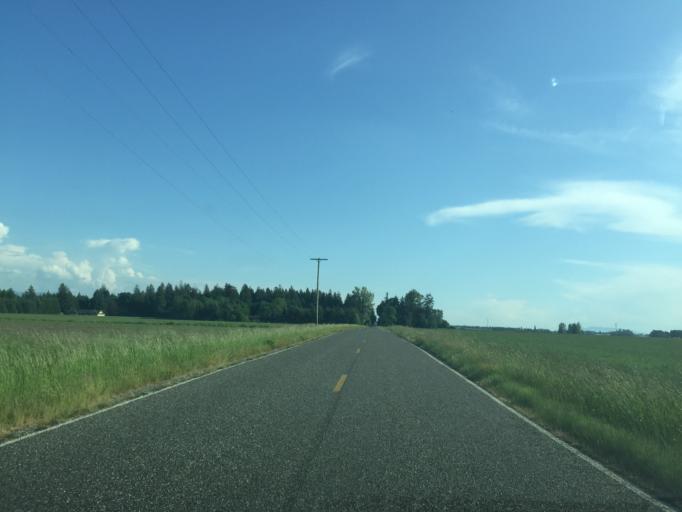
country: US
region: Washington
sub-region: Whatcom County
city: Lynden
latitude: 48.9841
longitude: -122.4627
